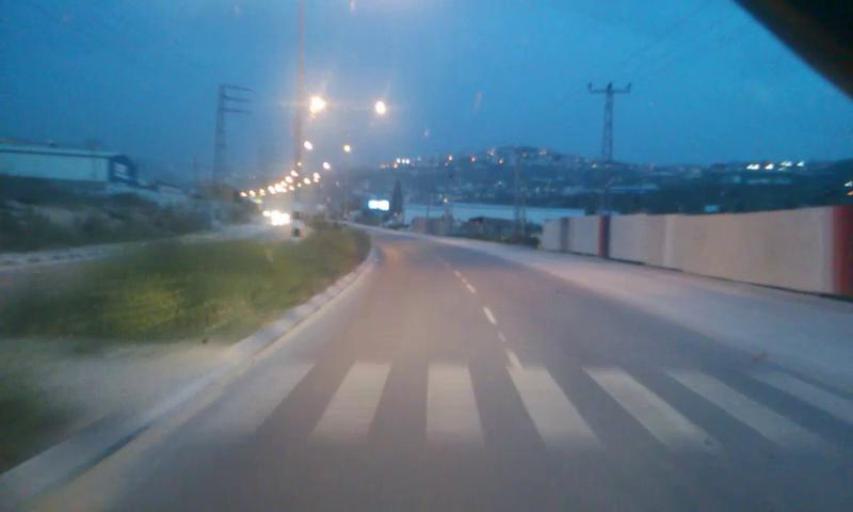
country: PS
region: West Bank
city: Dayr Sharaf
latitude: 32.2439
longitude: 35.1964
